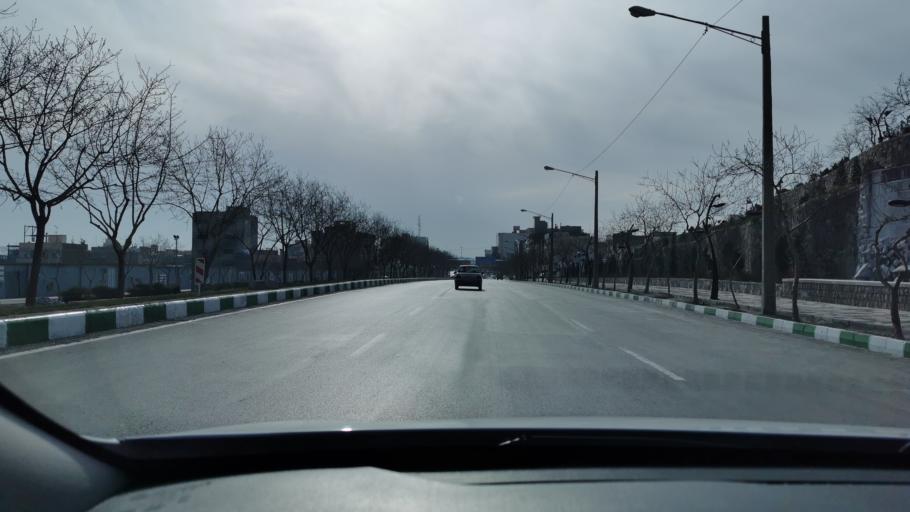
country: IR
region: Razavi Khorasan
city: Mashhad
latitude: 36.2946
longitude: 59.5314
